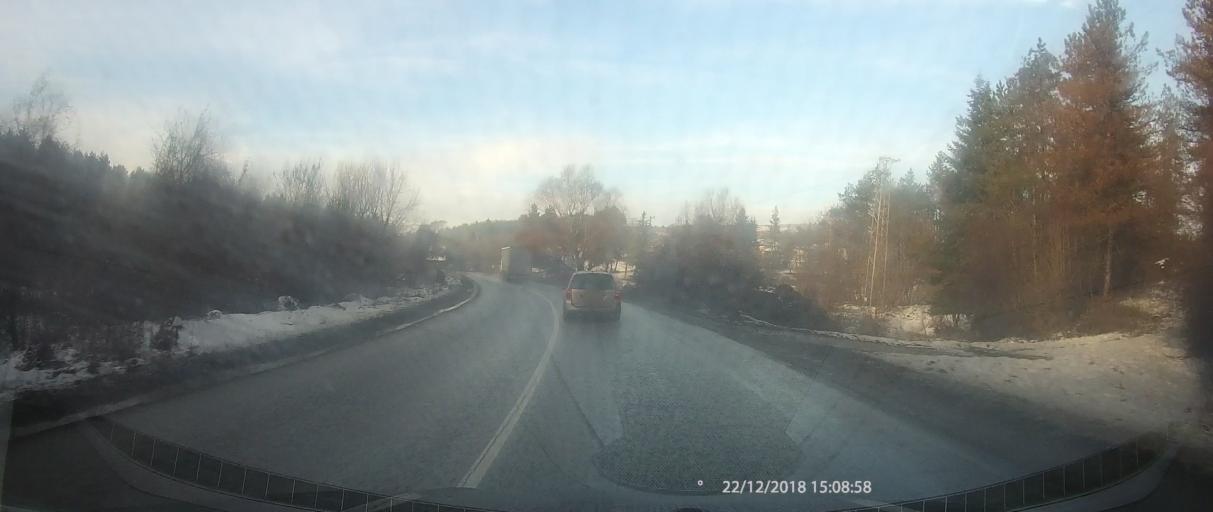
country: BG
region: Ruse
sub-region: Obshtina Borovo
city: Borovo
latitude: 43.4965
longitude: 25.8025
